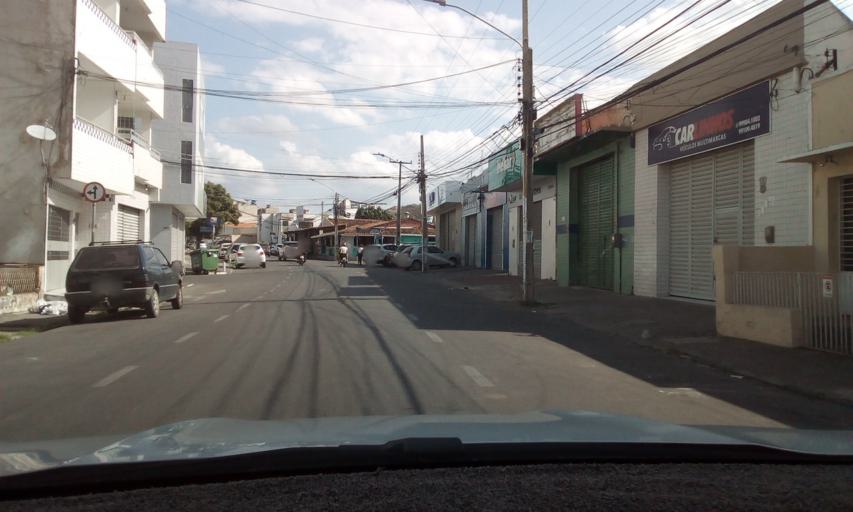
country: BR
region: Pernambuco
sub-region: Caruaru
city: Caruaru
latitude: -8.2766
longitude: -35.9754
